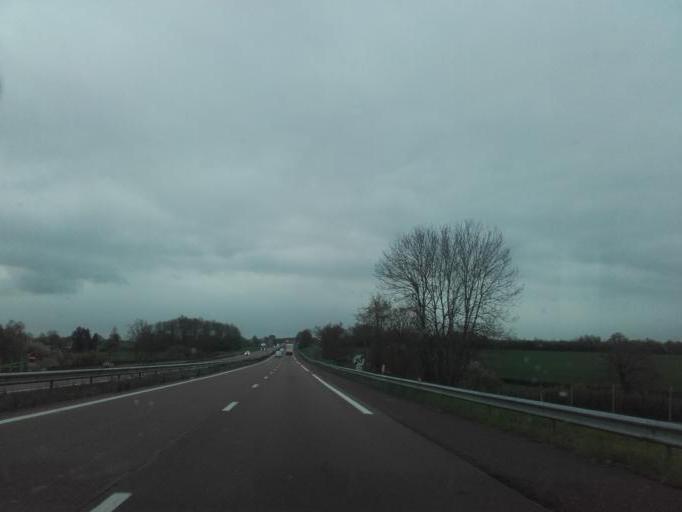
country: FR
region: Bourgogne
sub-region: Departement de l'Yonne
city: Avallon
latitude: 47.5431
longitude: 3.9720
